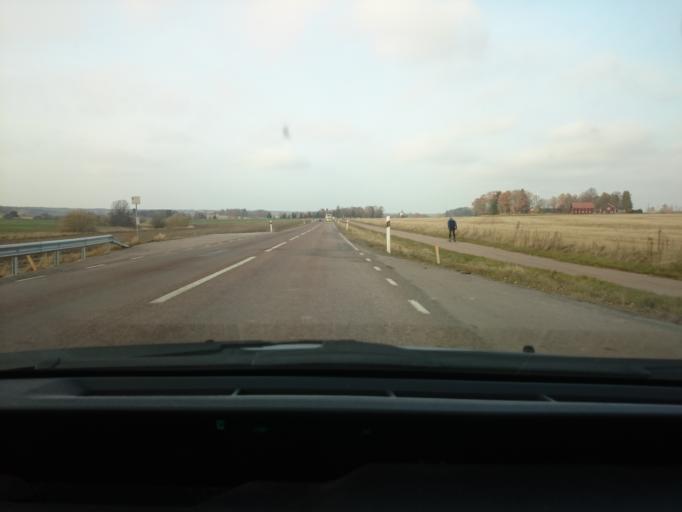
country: SE
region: Vaestmanland
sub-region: Vasteras
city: Skultuna
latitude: 59.6868
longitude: 16.4504
